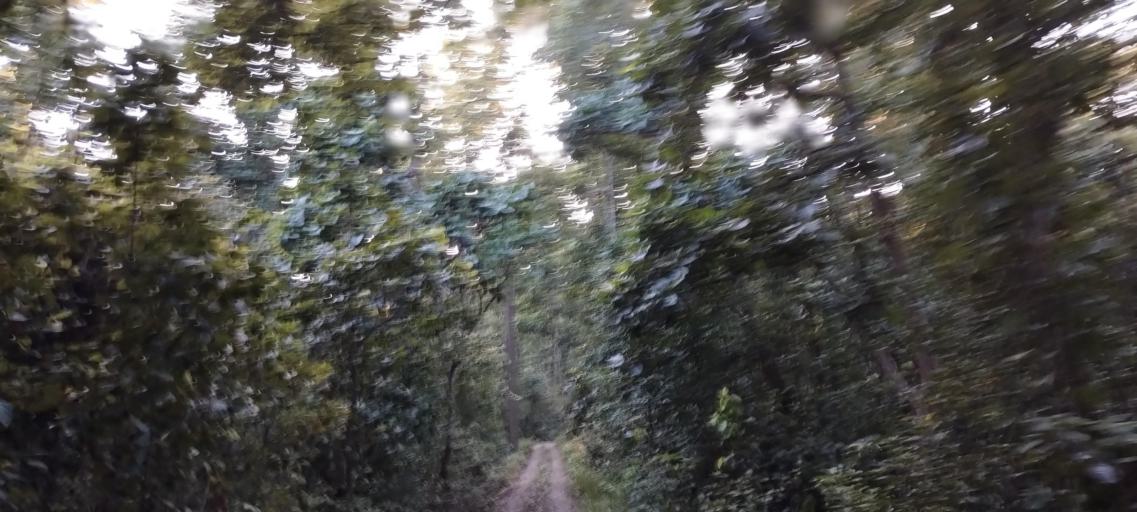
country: NP
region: Far Western
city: Tikapur
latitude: 28.4800
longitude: 81.2566
